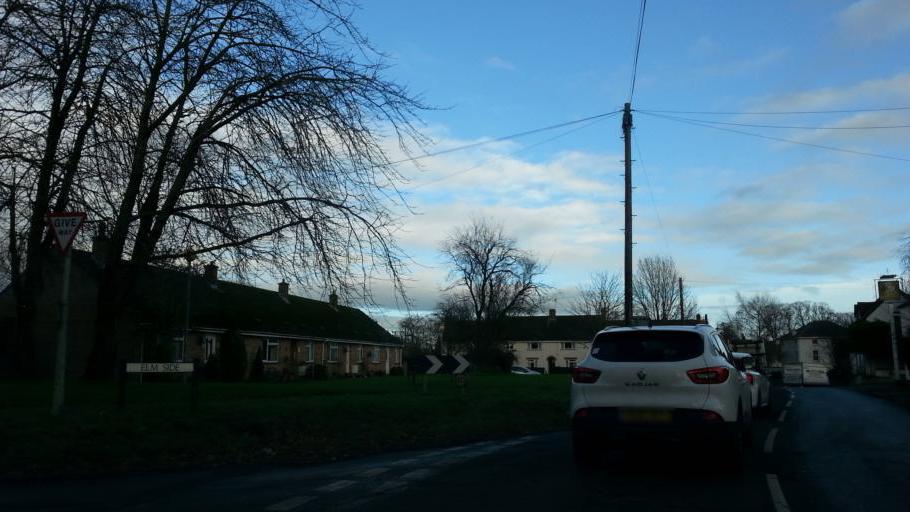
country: GB
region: England
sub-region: Oxfordshire
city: Faringdon
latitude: 51.6258
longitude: -1.5804
